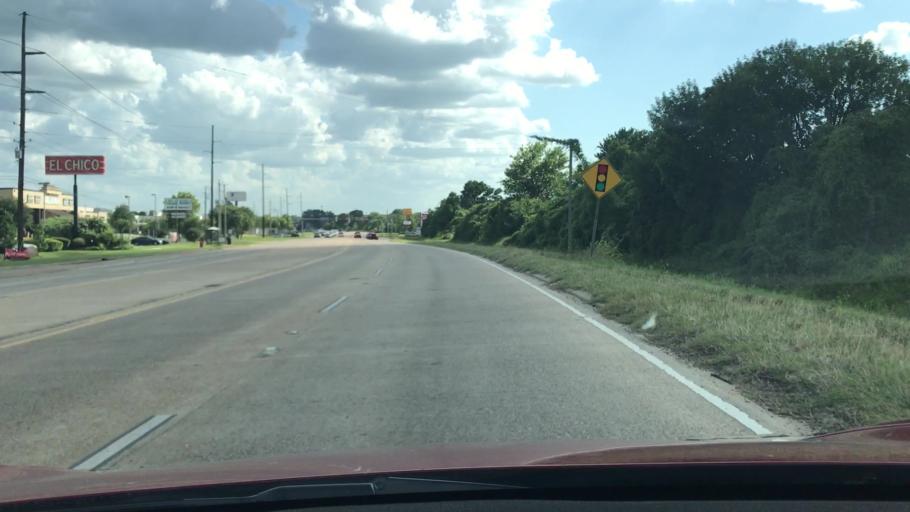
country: US
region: Louisiana
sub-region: Bossier Parish
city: Bossier City
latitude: 32.4298
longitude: -93.7159
